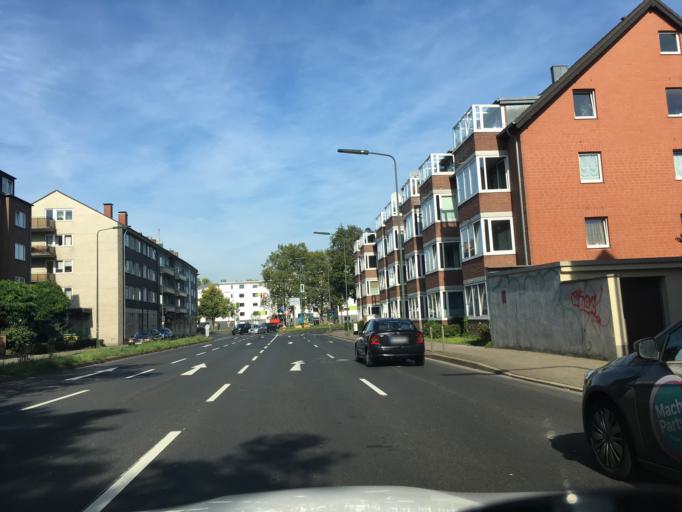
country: DE
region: North Rhine-Westphalia
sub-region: Regierungsbezirk Dusseldorf
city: Dusseldorf
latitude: 51.2042
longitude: 6.8323
